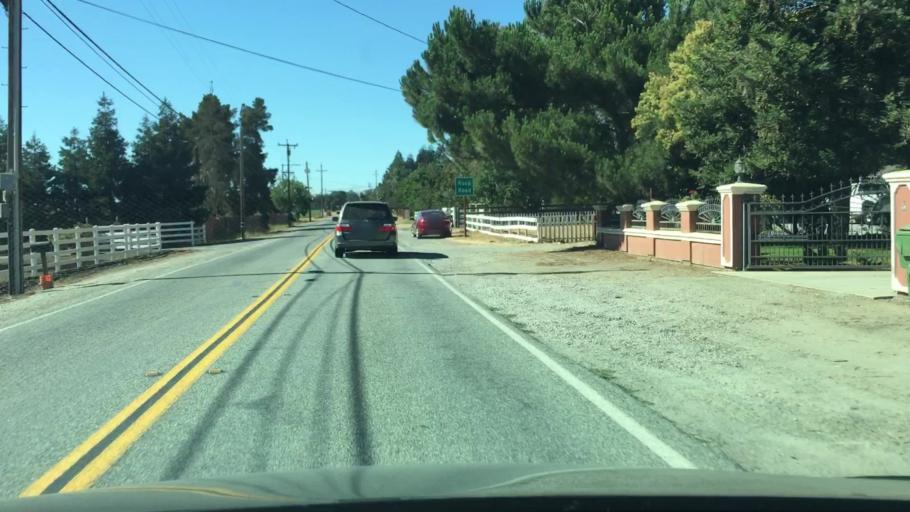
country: US
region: California
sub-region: Santa Clara County
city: Gilroy
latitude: 37.0400
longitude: -121.5410
